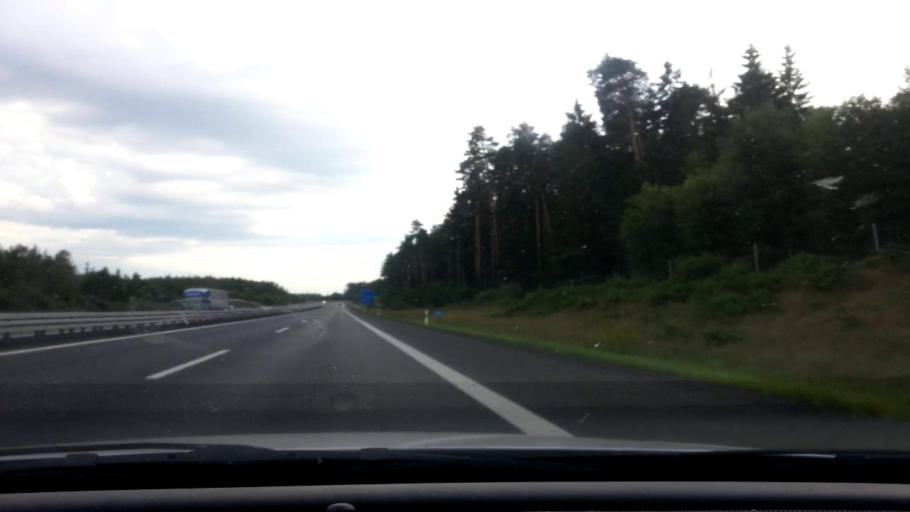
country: DE
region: Bavaria
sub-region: Upper Palatinate
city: Wiesau
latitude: 49.9203
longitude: 12.2226
